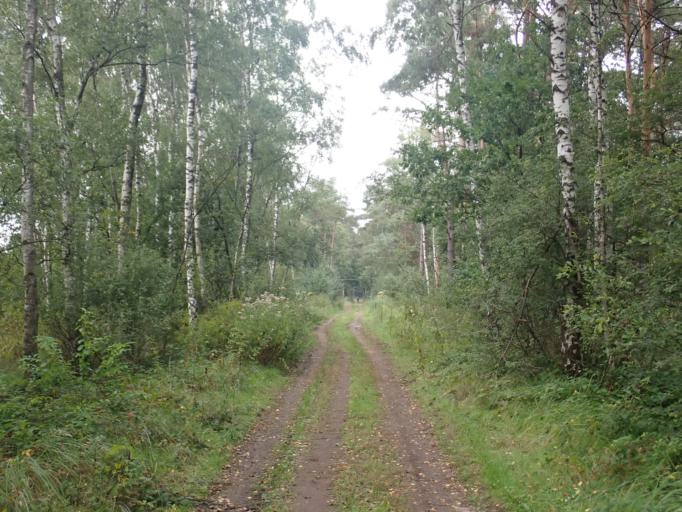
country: BE
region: Flanders
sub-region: Provincie Antwerpen
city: Kalmthout
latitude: 51.3433
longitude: 4.5053
